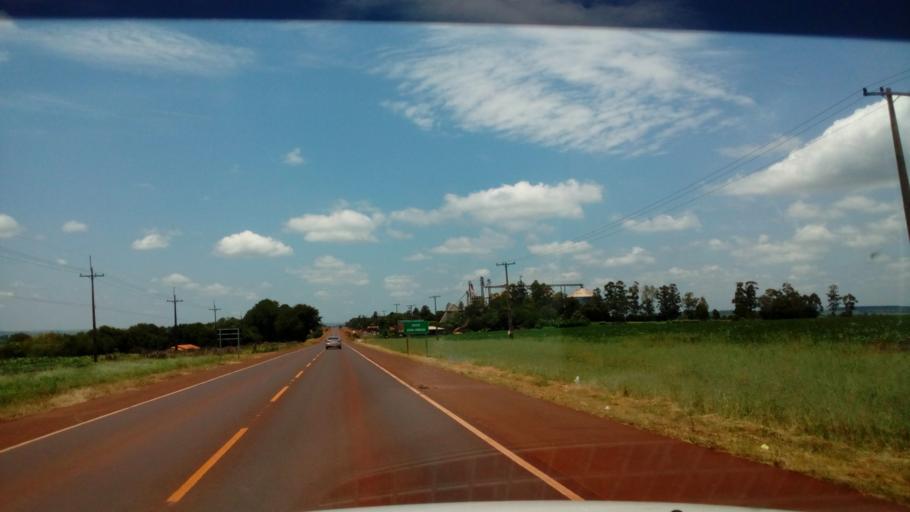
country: PY
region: Alto Parana
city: Naranjal
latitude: -26.0136
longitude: -55.1252
